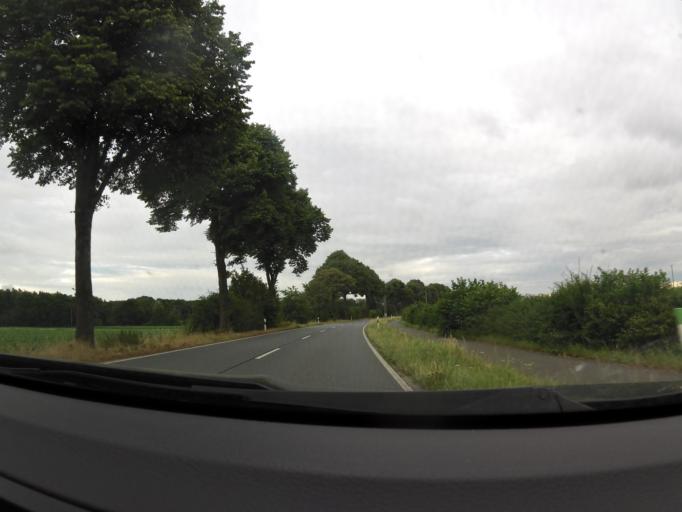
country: DE
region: North Rhine-Westphalia
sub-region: Regierungsbezirk Dusseldorf
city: Kevelaer
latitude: 51.5310
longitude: 6.2585
